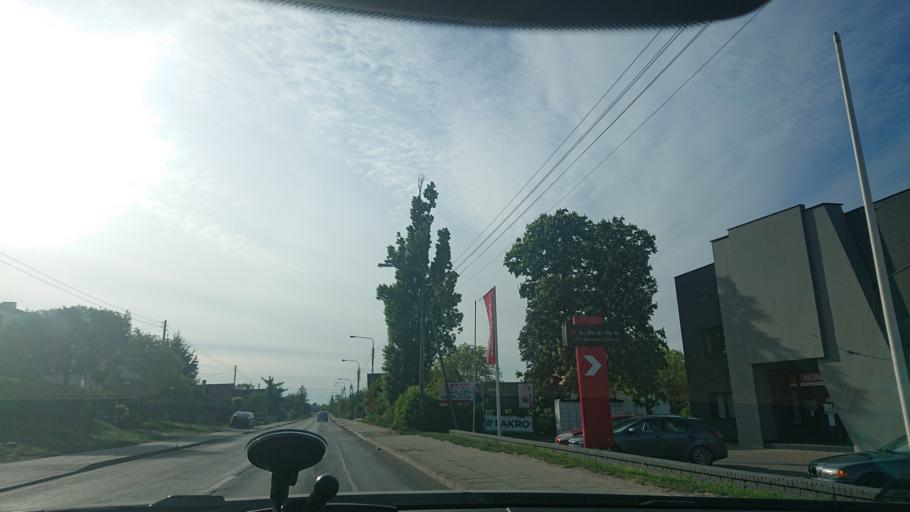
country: PL
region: Greater Poland Voivodeship
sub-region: Powiat gnieznienski
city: Gniezno
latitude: 52.5410
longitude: 17.5798
